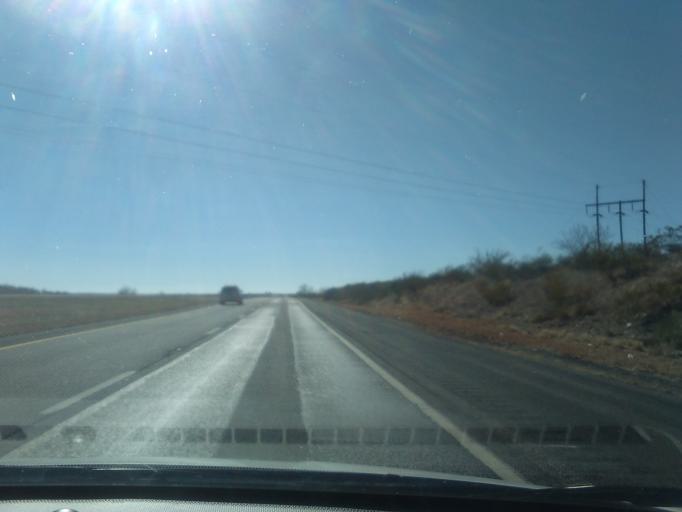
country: US
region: New Mexico
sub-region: Sierra County
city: Elephant Butte
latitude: 33.6065
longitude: -107.1530
